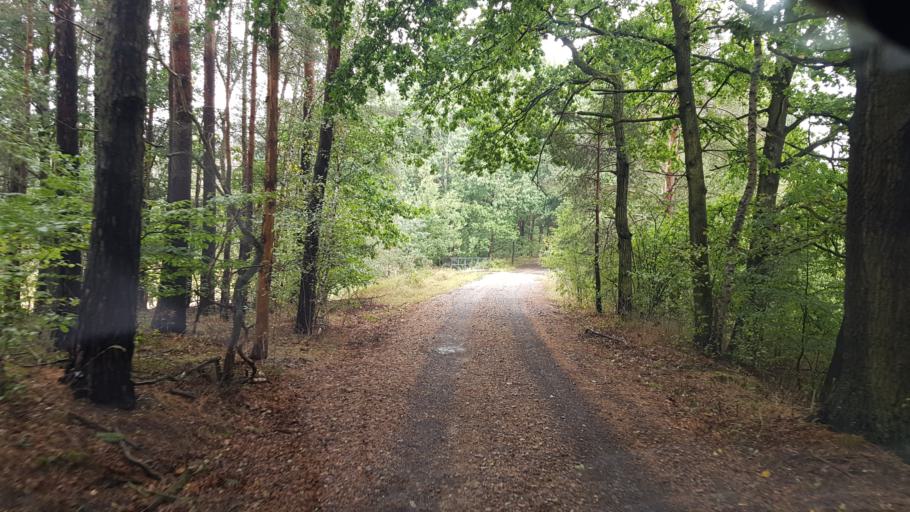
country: DE
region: Brandenburg
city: Ruckersdorf
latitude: 51.5522
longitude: 13.5730
